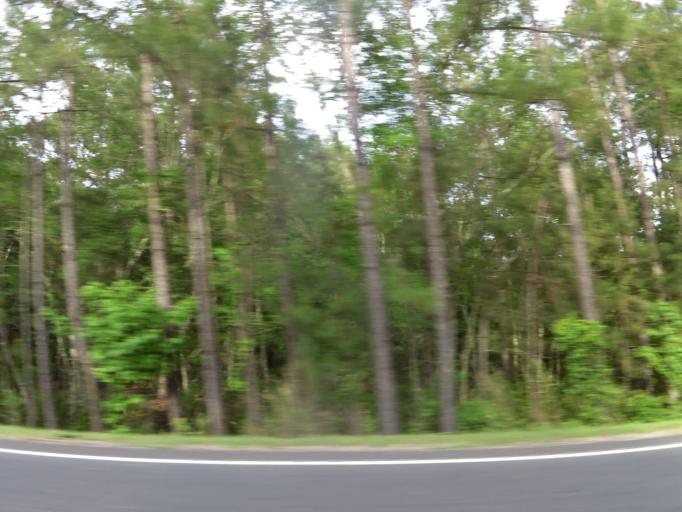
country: US
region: South Carolina
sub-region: Jasper County
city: Hardeeville
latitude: 32.3628
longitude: -81.0946
